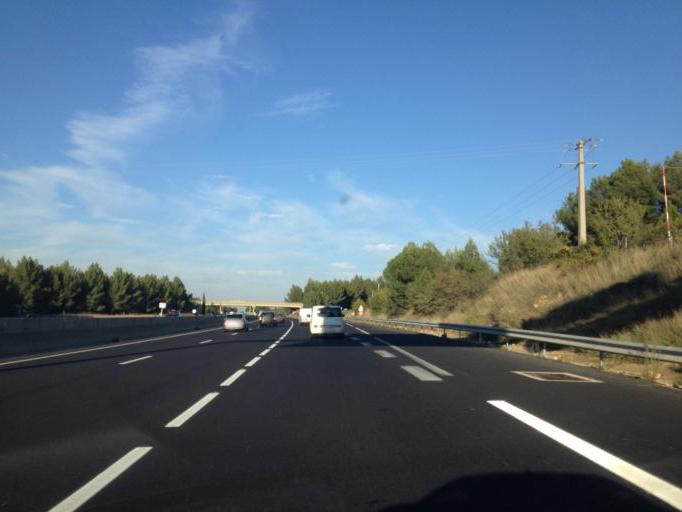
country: FR
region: Languedoc-Roussillon
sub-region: Departement de l'Herault
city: Lunel-Viel
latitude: 43.7005
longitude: 4.1131
